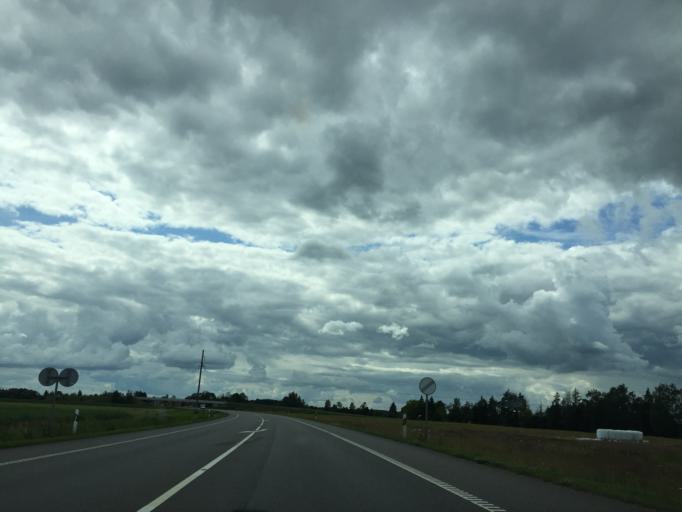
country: LT
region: Marijampoles apskritis
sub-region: Marijampole Municipality
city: Marijampole
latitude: 54.6325
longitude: 23.4310
